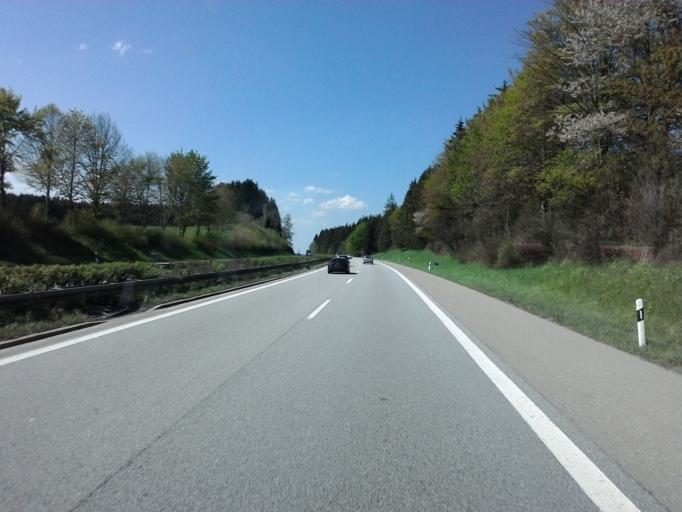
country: DE
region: Bavaria
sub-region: Swabia
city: Bohen
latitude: 47.8566
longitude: 10.2795
